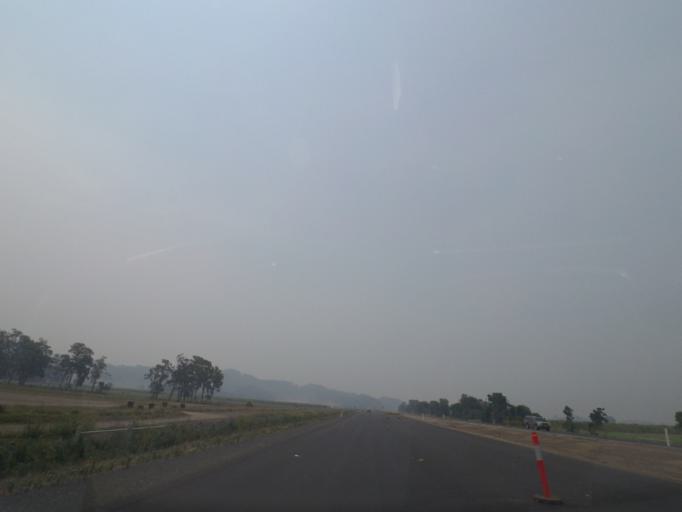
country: AU
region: New South Wales
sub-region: Ballina
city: Ballina
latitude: -28.8929
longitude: 153.4816
